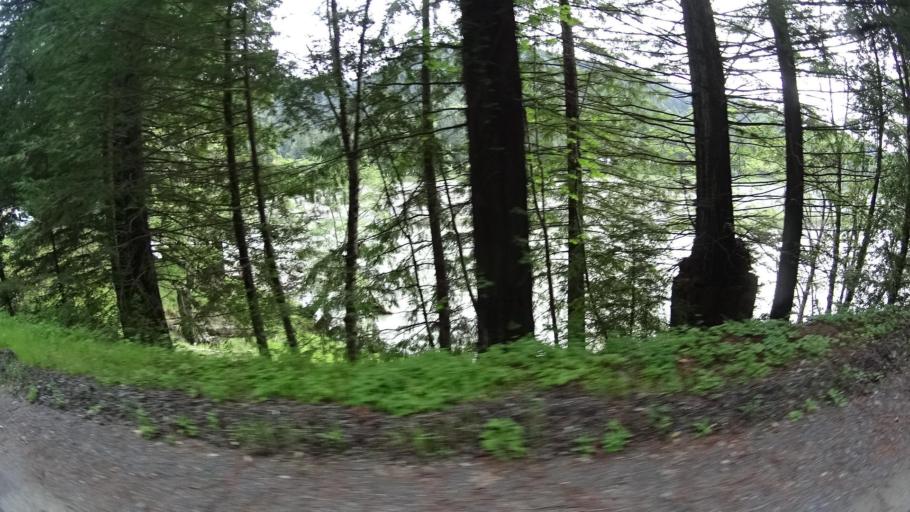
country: US
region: California
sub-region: Humboldt County
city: Redway
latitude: 40.3279
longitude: -123.8423
